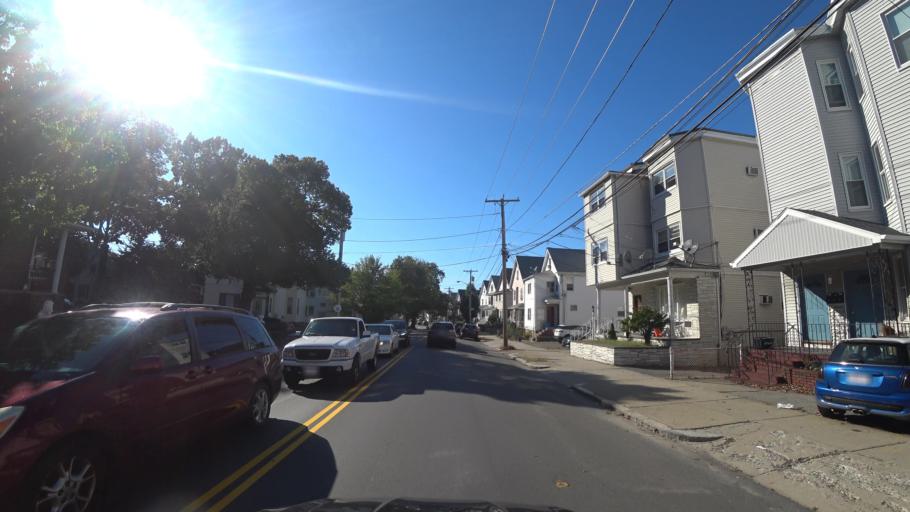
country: US
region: Massachusetts
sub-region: Middlesex County
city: Malden
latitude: 42.4182
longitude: -71.0657
